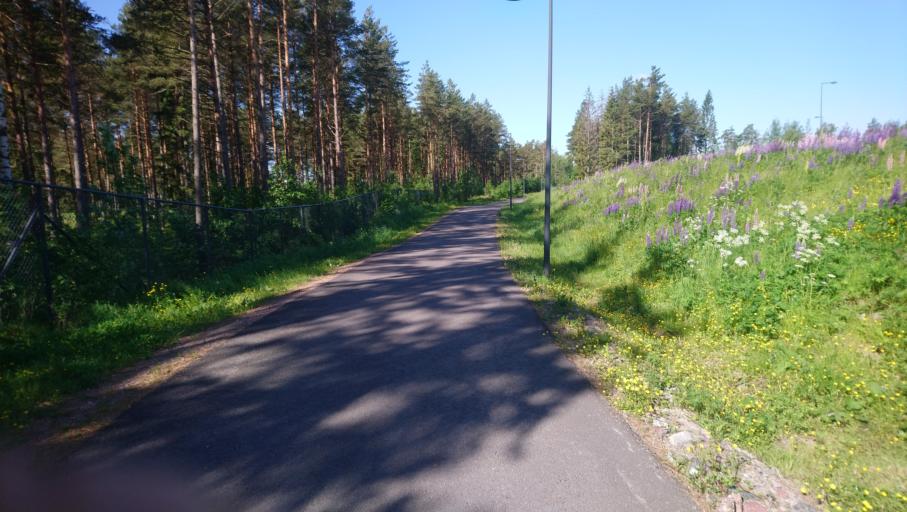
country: FI
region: Uusimaa
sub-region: Helsinki
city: Espoo
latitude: 60.1460
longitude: 24.5821
